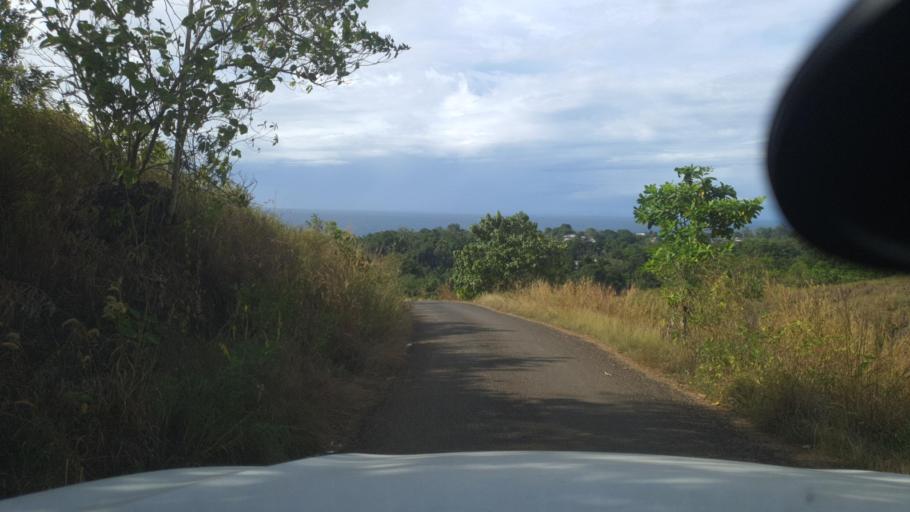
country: SB
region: Guadalcanal
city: Honiara
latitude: -9.4425
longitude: 159.9373
